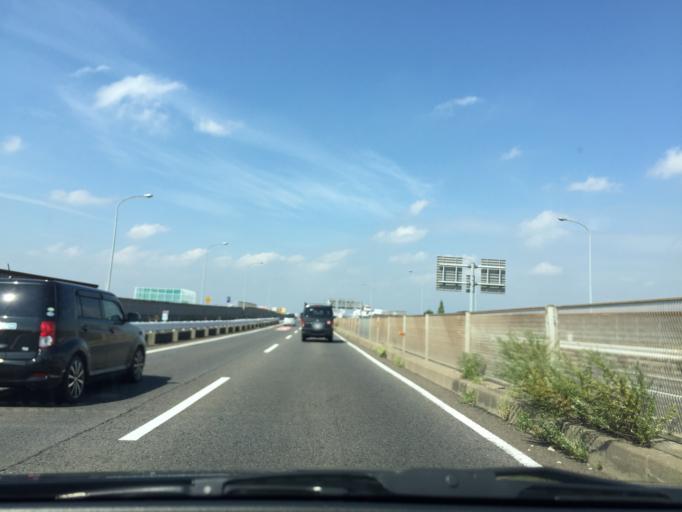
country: JP
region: Gifu
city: Kasamatsucho
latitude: 35.3883
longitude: 136.7790
